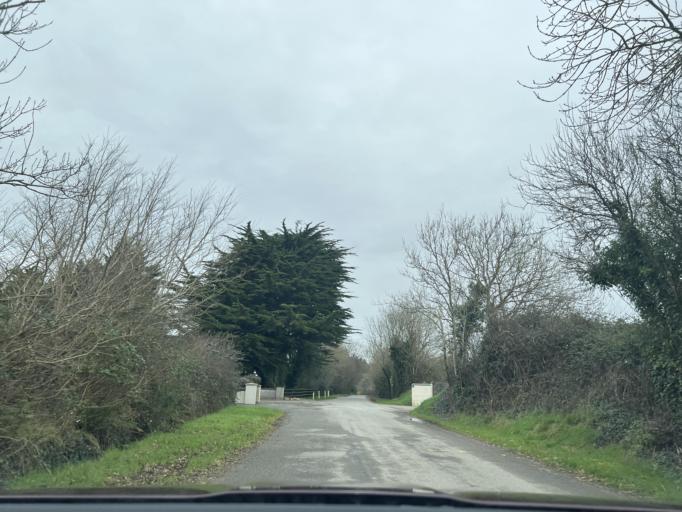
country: IE
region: Leinster
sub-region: Loch Garman
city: Loch Garman
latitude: 52.3652
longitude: -6.5206
